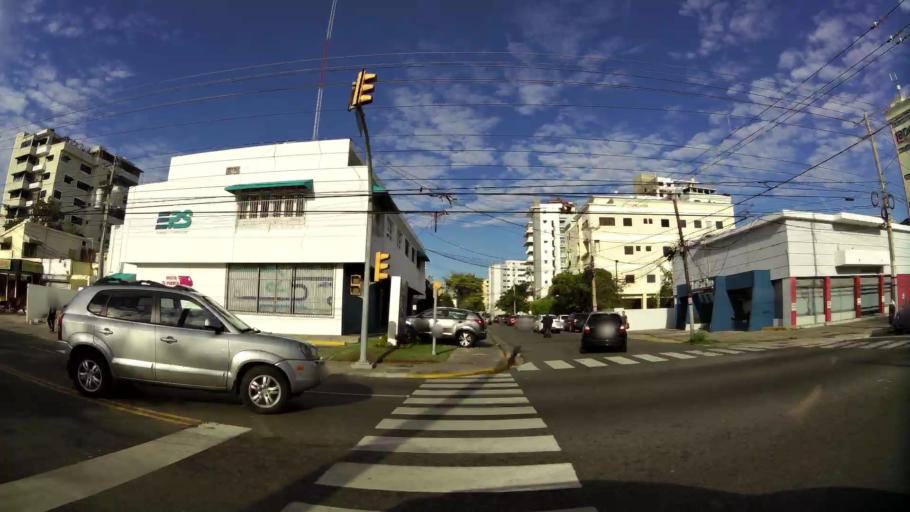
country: DO
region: Nacional
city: La Julia
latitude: 18.4779
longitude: -69.9205
